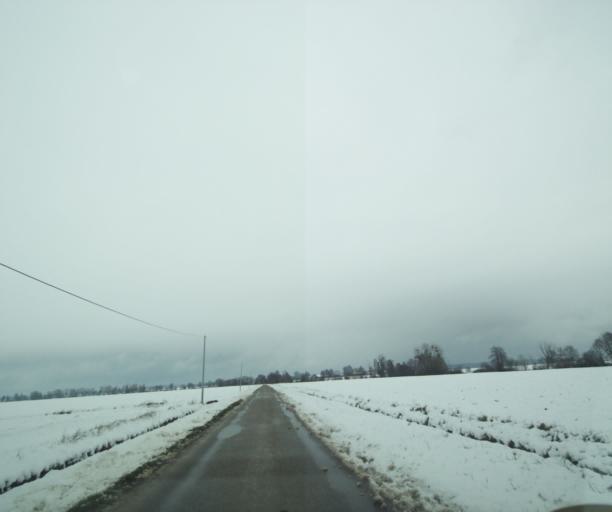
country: FR
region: Champagne-Ardenne
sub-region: Departement de la Haute-Marne
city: Montier-en-Der
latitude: 48.4308
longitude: 4.7904
